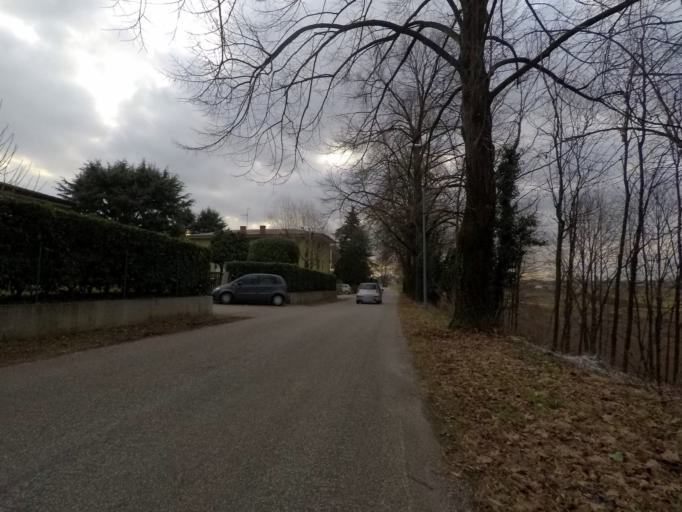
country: IT
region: Friuli Venezia Giulia
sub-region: Provincia di Udine
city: Tavagnacco
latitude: 46.1214
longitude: 13.2112
